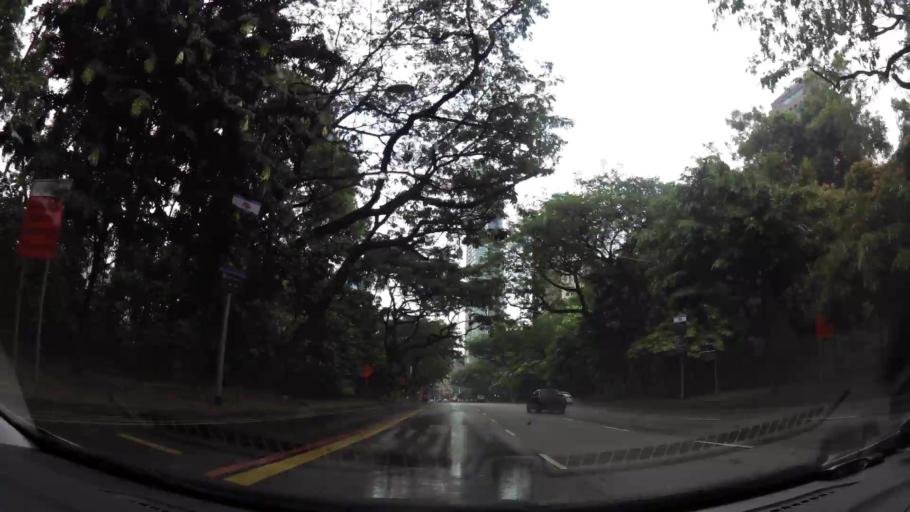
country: SG
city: Singapore
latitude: 1.3013
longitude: 103.8337
